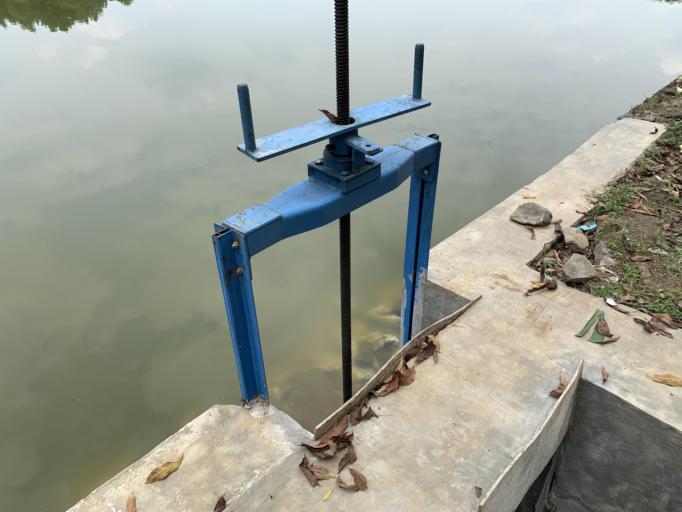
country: ID
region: West Java
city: Serpong
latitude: -6.4069
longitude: 106.5865
